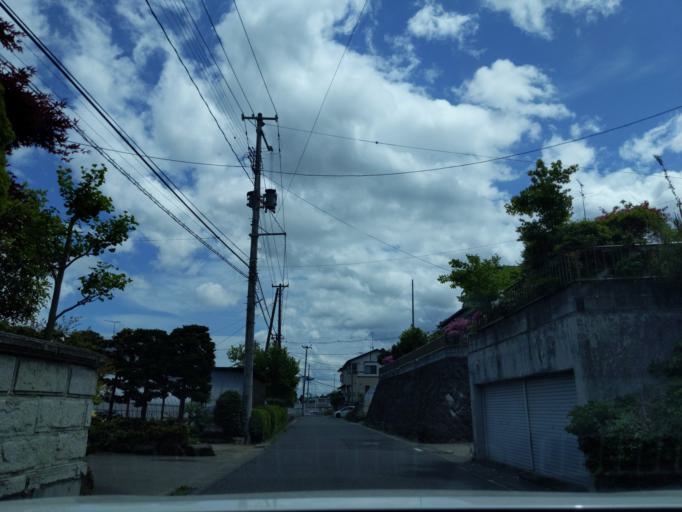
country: JP
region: Fukushima
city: Sukagawa
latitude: 37.3001
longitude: 140.3649
